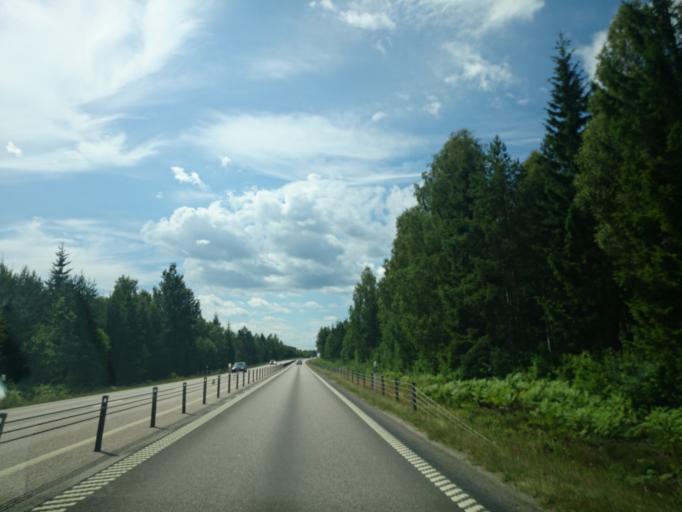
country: SE
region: Kalmar
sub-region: Monsteras Kommun
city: Timmernabben
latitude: 56.9935
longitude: 16.4123
